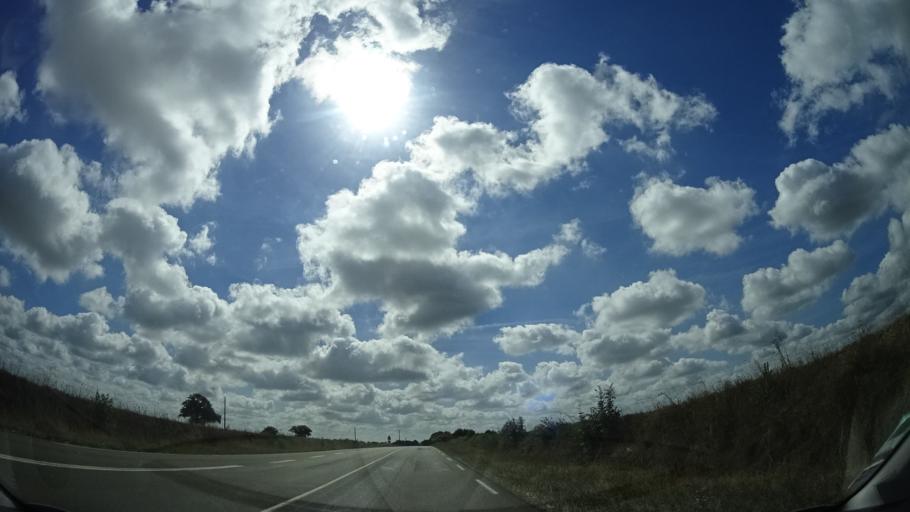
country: FR
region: Pays de la Loire
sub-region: Departement de la Mayenne
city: Entrammes
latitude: 48.0043
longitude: -0.6526
